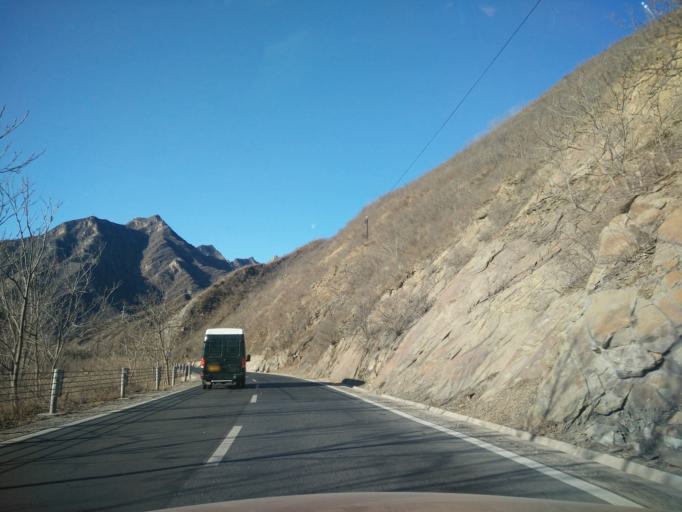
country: CN
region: Beijing
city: Miaofengshan
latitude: 40.0056
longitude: 116.0243
